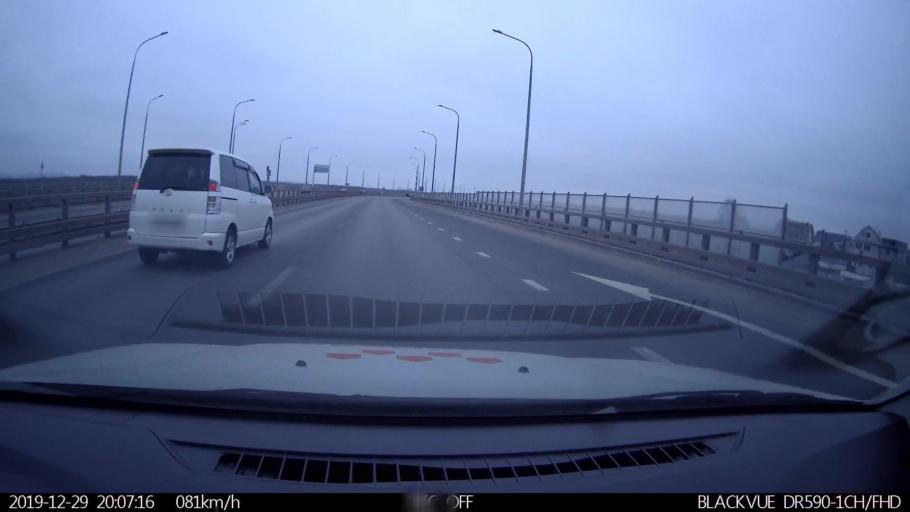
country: RU
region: Nizjnij Novgorod
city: Neklyudovo
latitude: 56.3955
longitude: 43.9870
